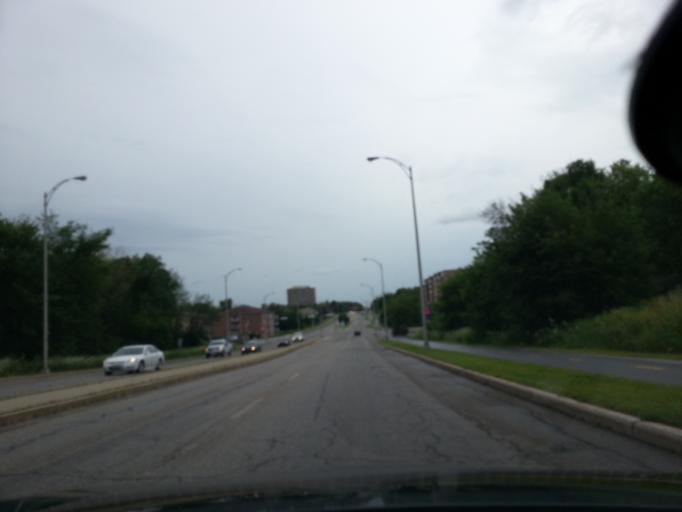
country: CA
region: Ontario
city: Ottawa
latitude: 45.4316
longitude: -75.7627
